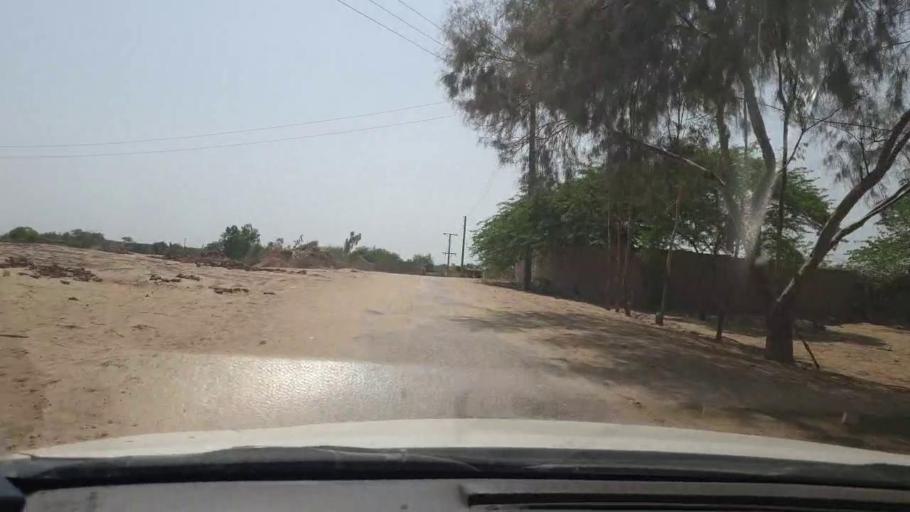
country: PK
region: Sindh
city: Rohri
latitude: 27.5221
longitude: 69.0571
